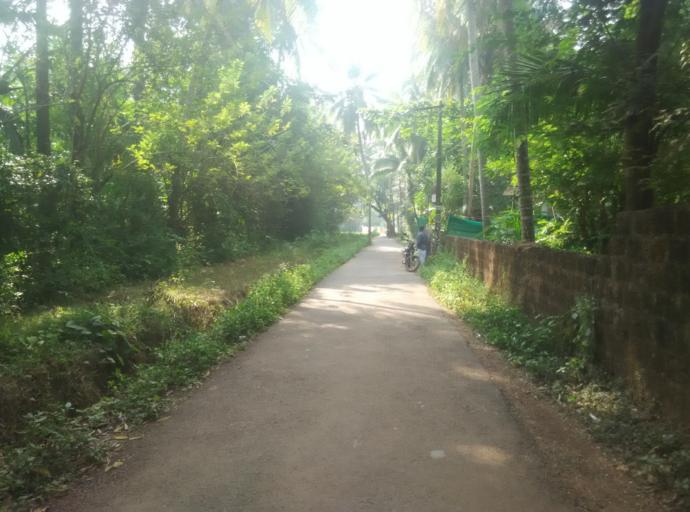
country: IN
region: Kerala
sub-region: Kozhikode
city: Kunnamangalam
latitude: 11.2921
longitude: 75.8297
